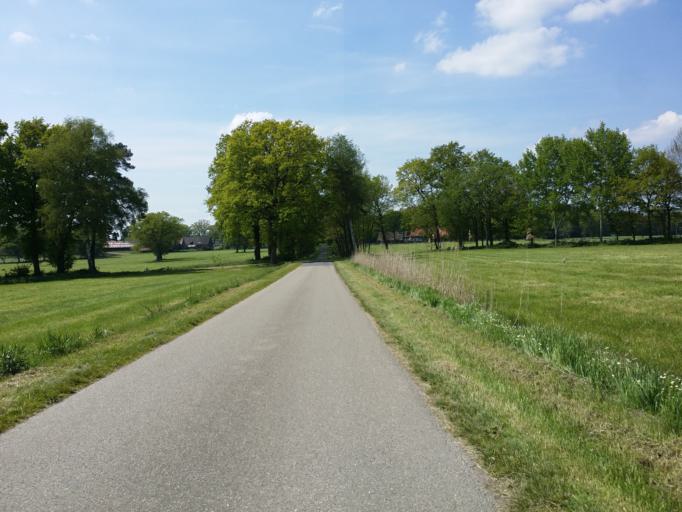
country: DE
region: Lower Saxony
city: Wulsbuttel
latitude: 53.2930
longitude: 8.6743
